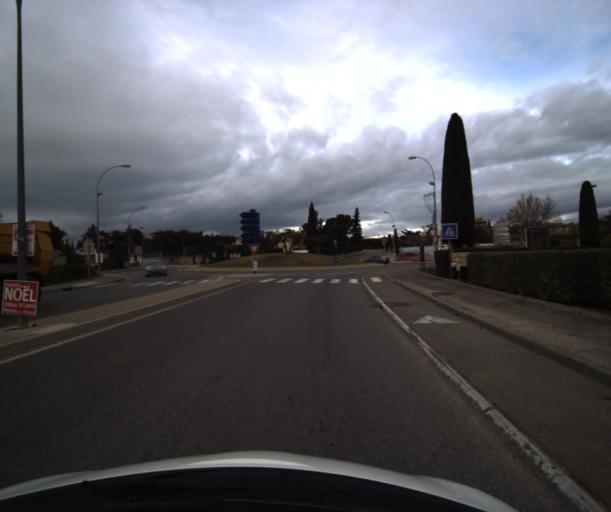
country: FR
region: Provence-Alpes-Cote d'Azur
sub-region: Departement du Vaucluse
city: Pertuis
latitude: 43.6938
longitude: 5.4899
